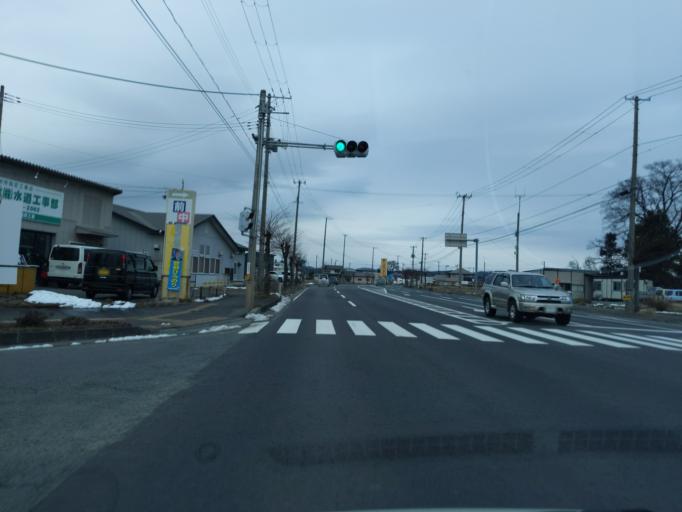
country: JP
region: Iwate
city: Mizusawa
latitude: 39.1762
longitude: 141.1593
